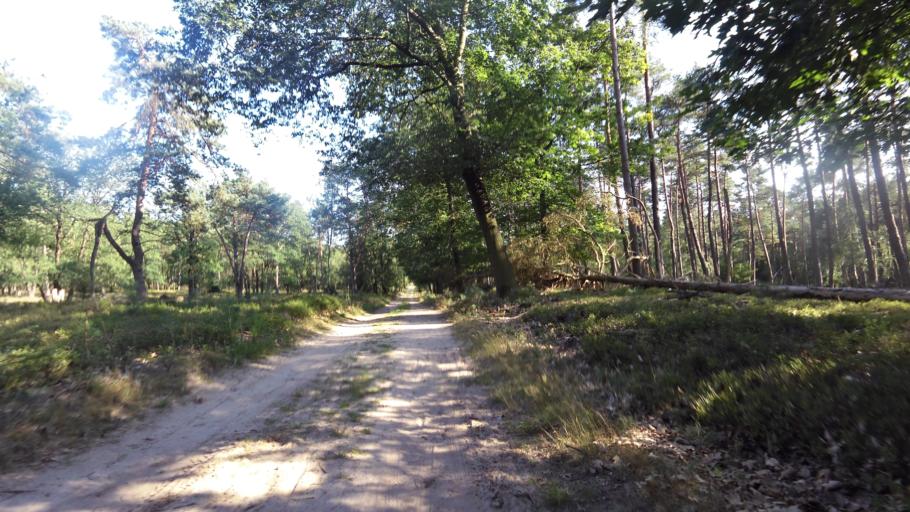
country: NL
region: Gelderland
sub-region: Gemeente Apeldoorn
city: Loenen
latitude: 52.1142
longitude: 5.9792
